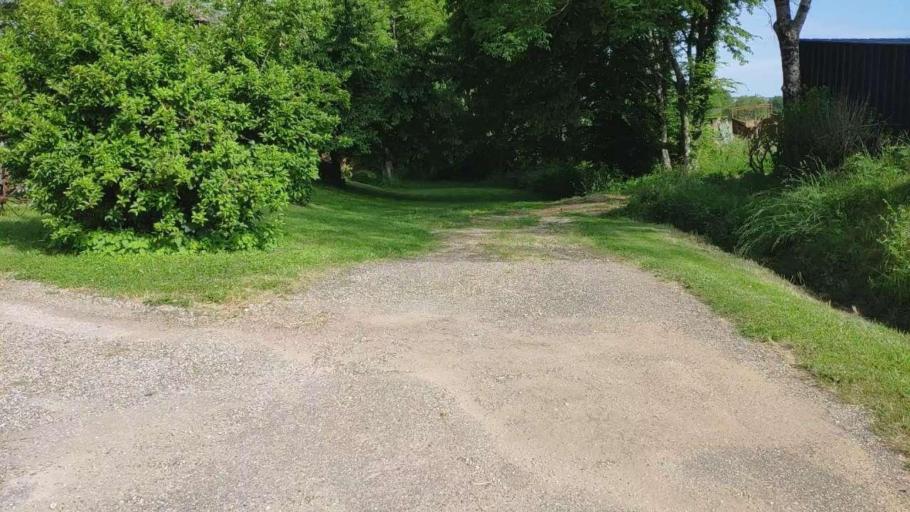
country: FR
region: Franche-Comte
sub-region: Departement du Jura
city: Bletterans
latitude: 46.7159
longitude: 5.4560
